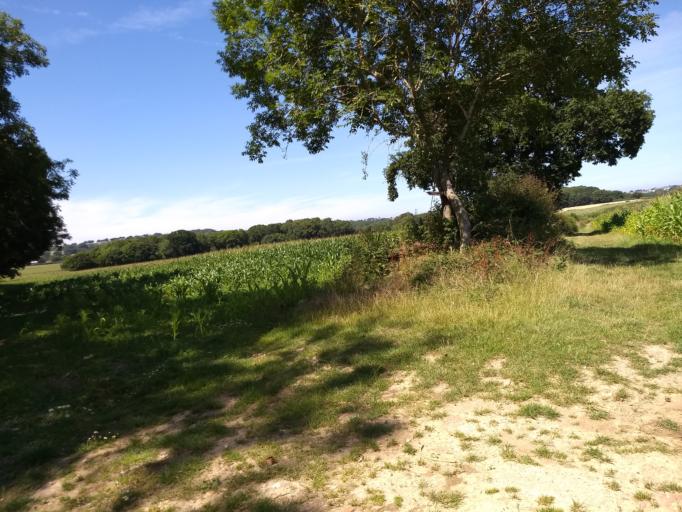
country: GB
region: England
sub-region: Isle of Wight
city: Brading
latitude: 50.6948
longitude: -1.1601
